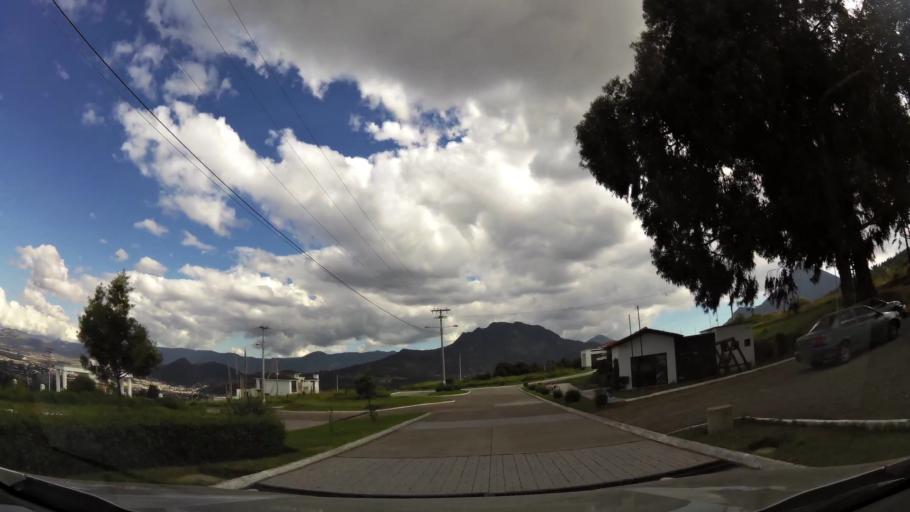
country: GT
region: Quetzaltenango
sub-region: Municipio de La Esperanza
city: La Esperanza
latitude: 14.8347
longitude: -91.5570
